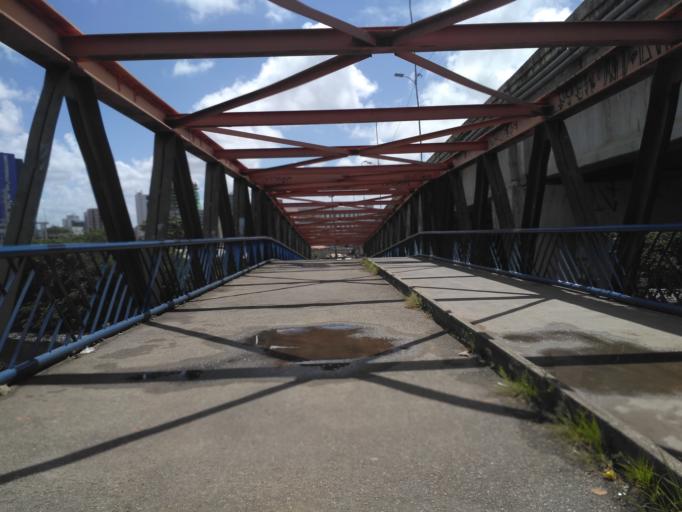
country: BR
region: Pernambuco
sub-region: Recife
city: Recife
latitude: -8.0704
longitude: -34.8907
